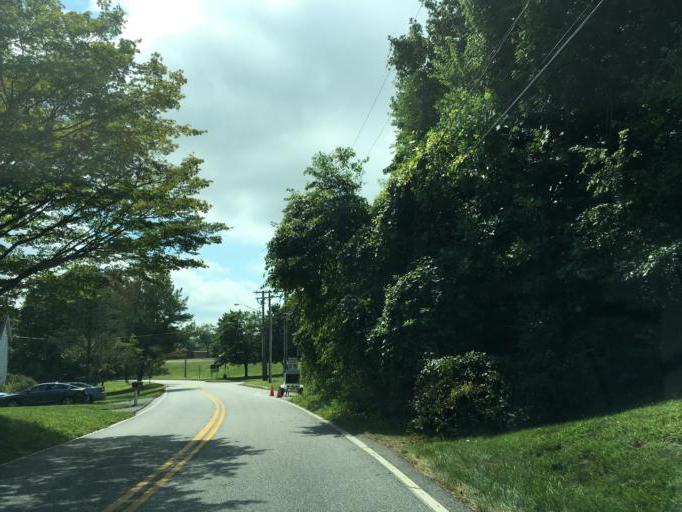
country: US
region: Maryland
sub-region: Anne Arundel County
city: Crownsville
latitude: 39.0274
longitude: -76.6045
